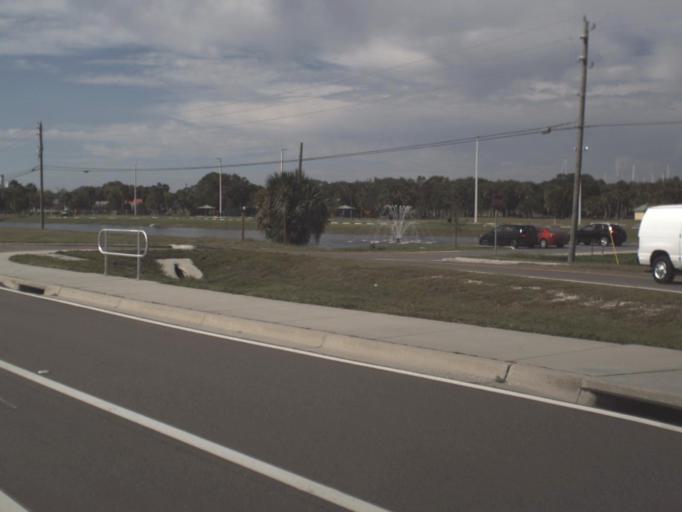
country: US
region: Florida
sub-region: Brevard County
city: Titusville
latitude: 28.6172
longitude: -80.8034
